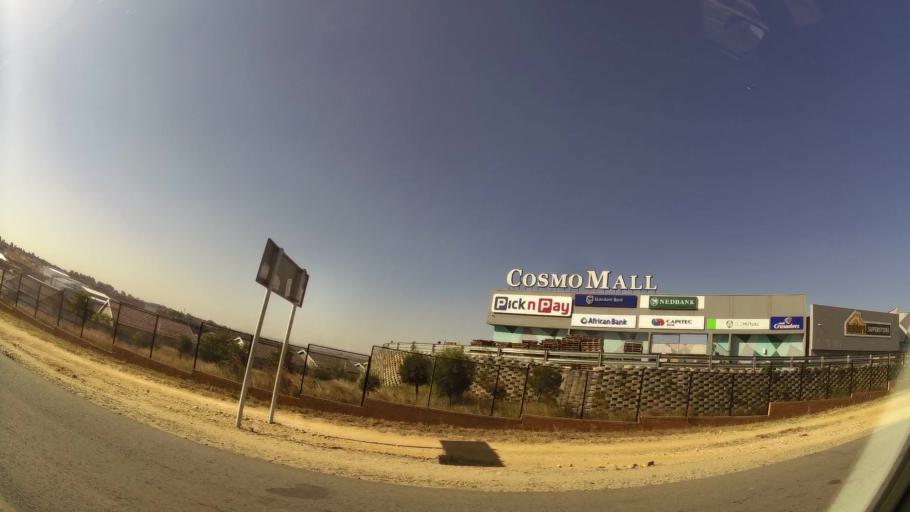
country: ZA
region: Gauteng
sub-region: West Rand District Municipality
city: Muldersdriseloop
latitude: -26.0130
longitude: 27.9381
